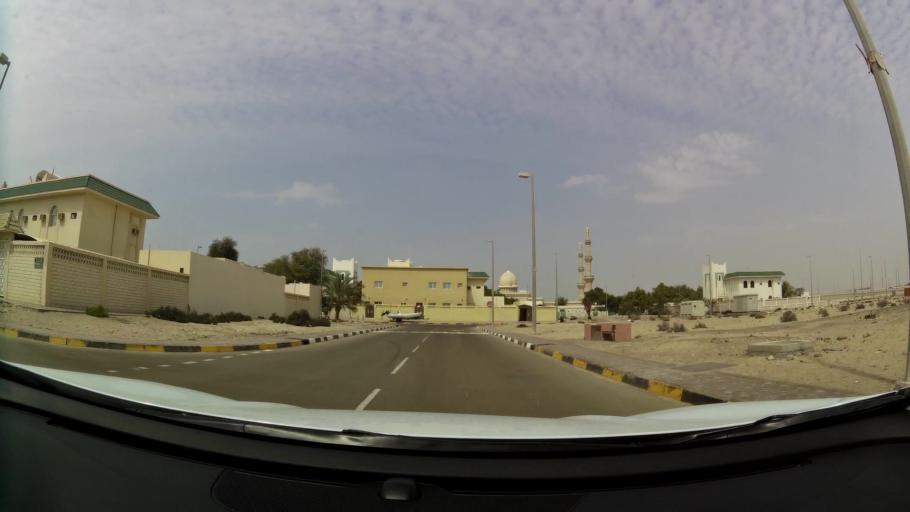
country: AE
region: Abu Dhabi
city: Abu Dhabi
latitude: 24.5399
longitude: 54.6911
